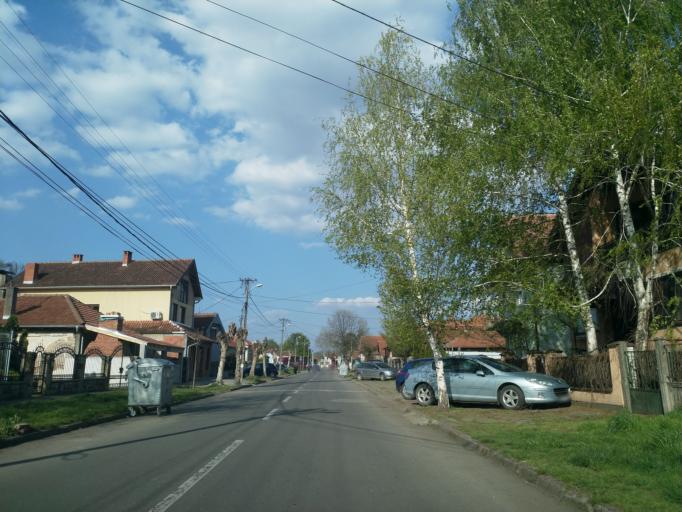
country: RS
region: Central Serbia
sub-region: Pomoravski Okrug
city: Cuprija
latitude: 43.9188
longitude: 21.3716
